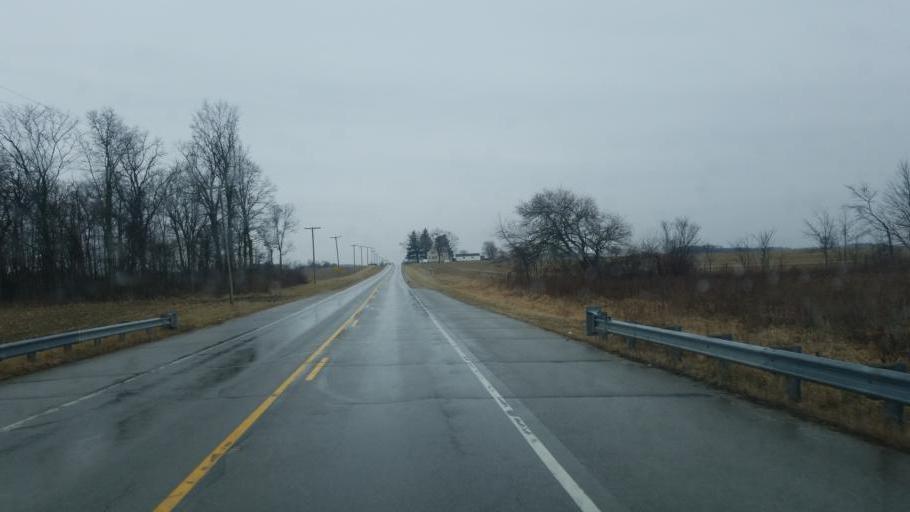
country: US
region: Indiana
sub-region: Adams County
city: Berne
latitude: 40.6349
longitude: -85.0414
